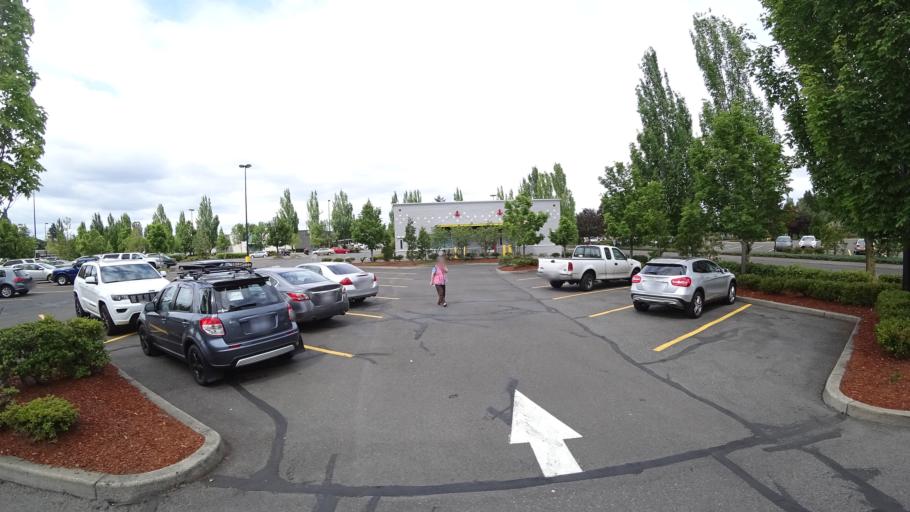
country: US
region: Oregon
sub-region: Multnomah County
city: Lents
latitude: 45.4933
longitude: -122.5765
